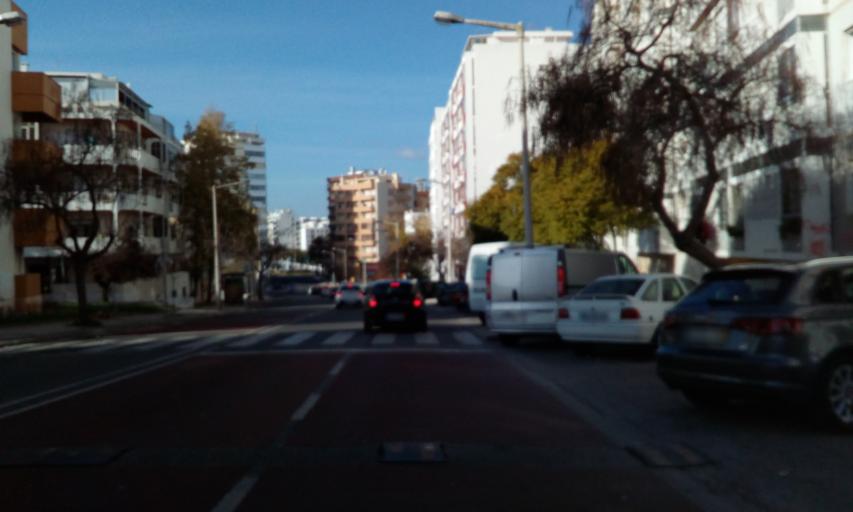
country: PT
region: Faro
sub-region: Faro
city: Faro
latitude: 37.0223
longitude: -7.9246
